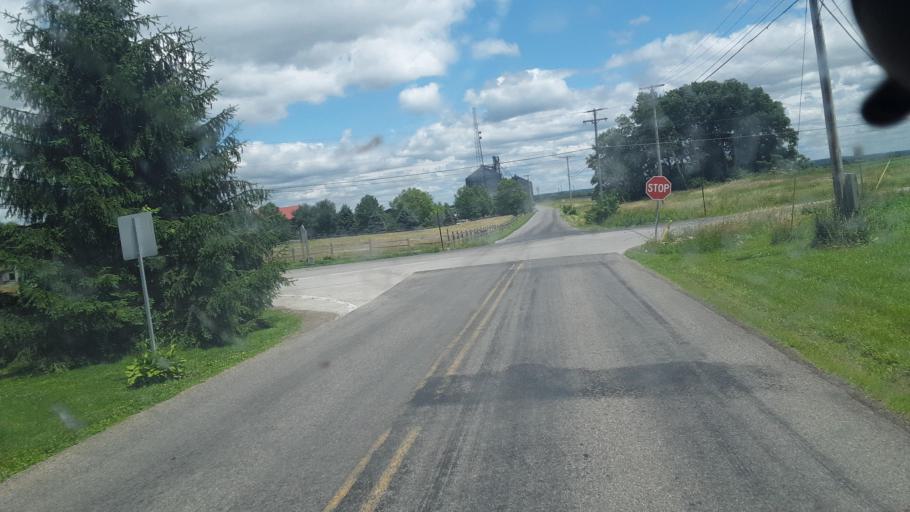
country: US
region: Pennsylvania
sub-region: Lawrence County
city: New Wilmington
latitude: 41.1014
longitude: -80.2164
